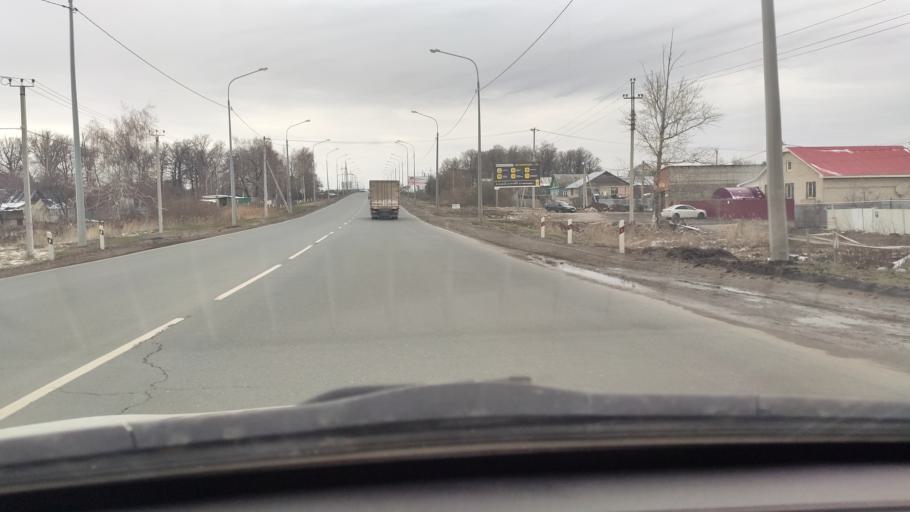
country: RU
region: Samara
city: Zhigulevsk
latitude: 53.3745
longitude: 49.4567
